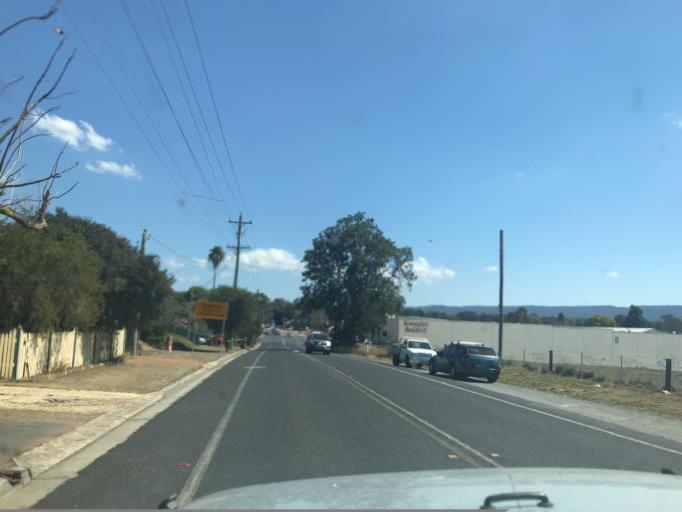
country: AU
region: New South Wales
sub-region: Hawkesbury
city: Richmond
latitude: -33.5787
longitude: 150.7220
